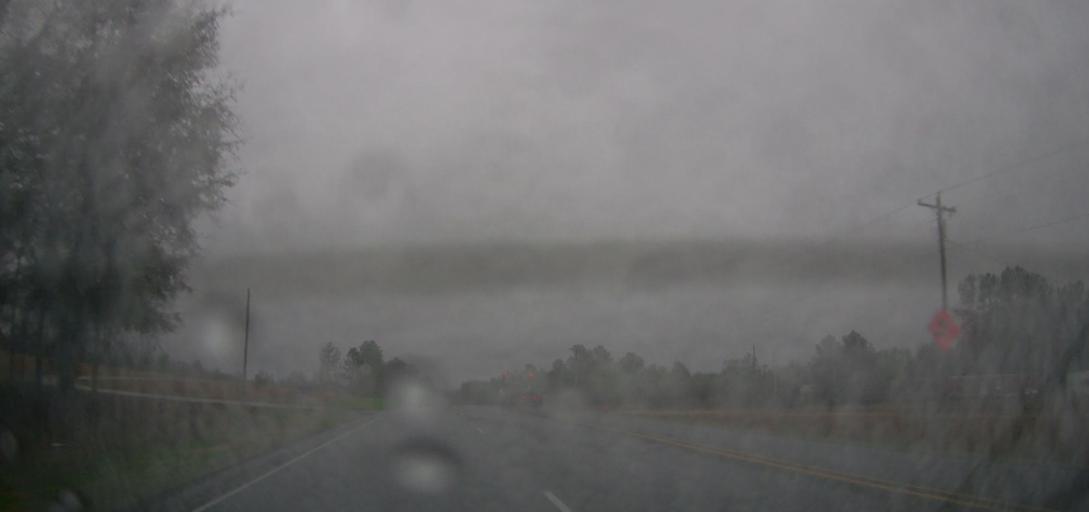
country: US
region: Alabama
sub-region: Autauga County
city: Pine Level
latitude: 32.5844
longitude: -86.6944
